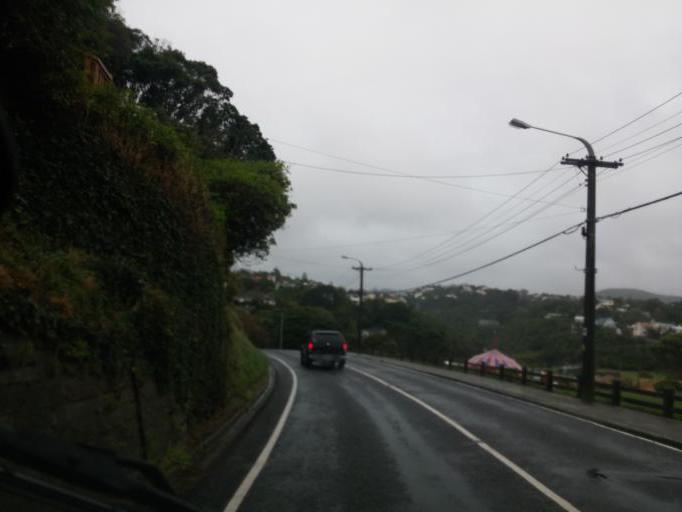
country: NZ
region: Wellington
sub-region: Wellington City
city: Kelburn
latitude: -41.2773
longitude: 174.7556
